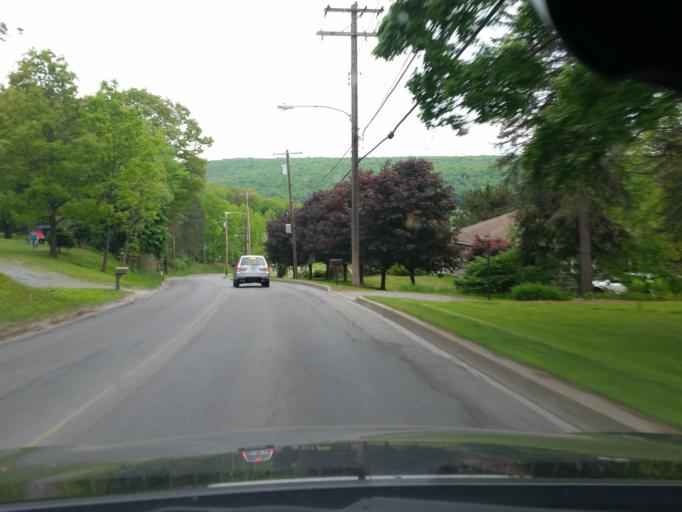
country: US
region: Pennsylvania
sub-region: Elk County
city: Ridgway
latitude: 41.4278
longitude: -78.7395
